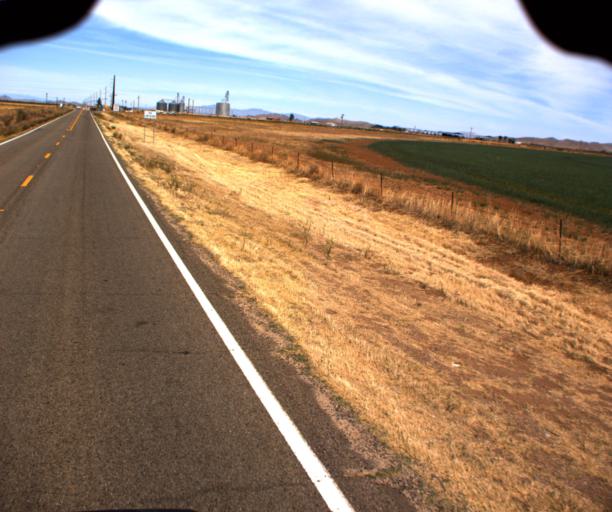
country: US
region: Arizona
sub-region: Cochise County
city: Tombstone
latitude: 31.7553
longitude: -109.6892
